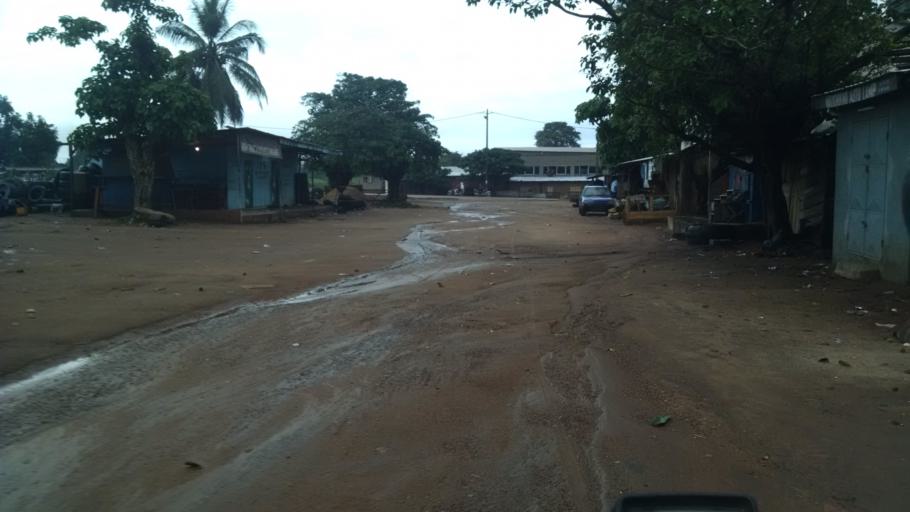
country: CI
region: Vallee du Bandama
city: Bouake
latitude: 7.6840
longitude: -5.0375
